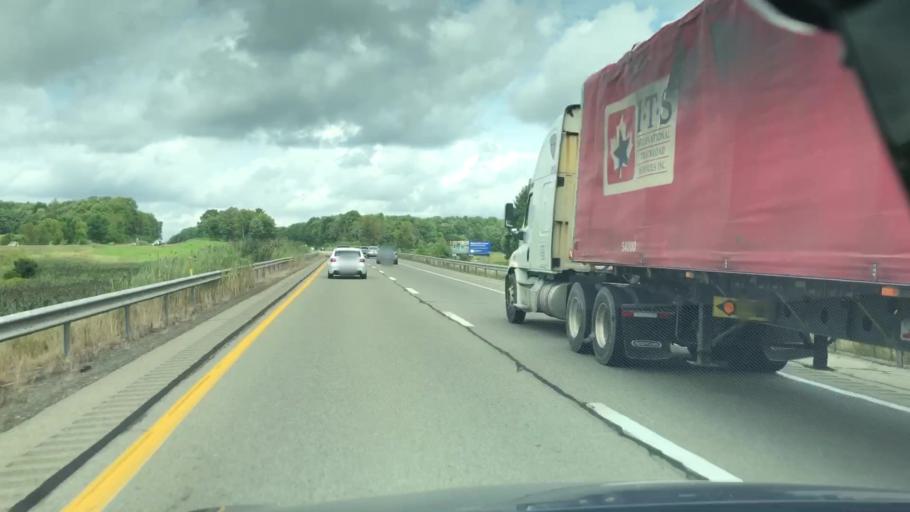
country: US
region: Pennsylvania
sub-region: Erie County
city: Edinboro
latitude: 41.7807
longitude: -80.1820
